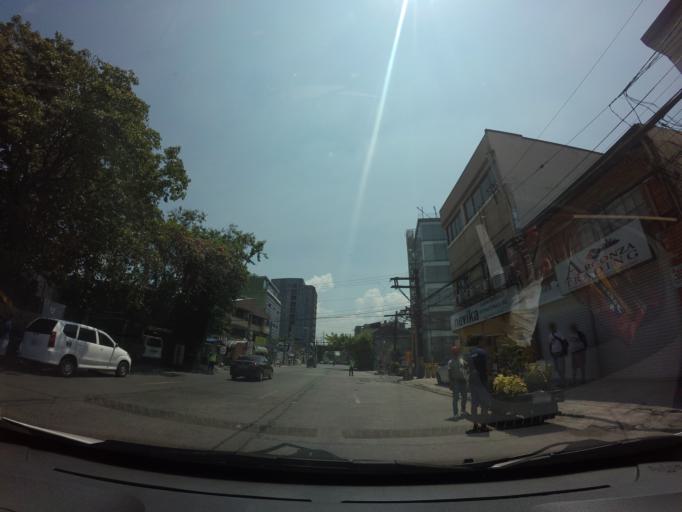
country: PH
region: Metro Manila
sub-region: Makati City
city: Makati City
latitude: 14.5647
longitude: 121.0018
